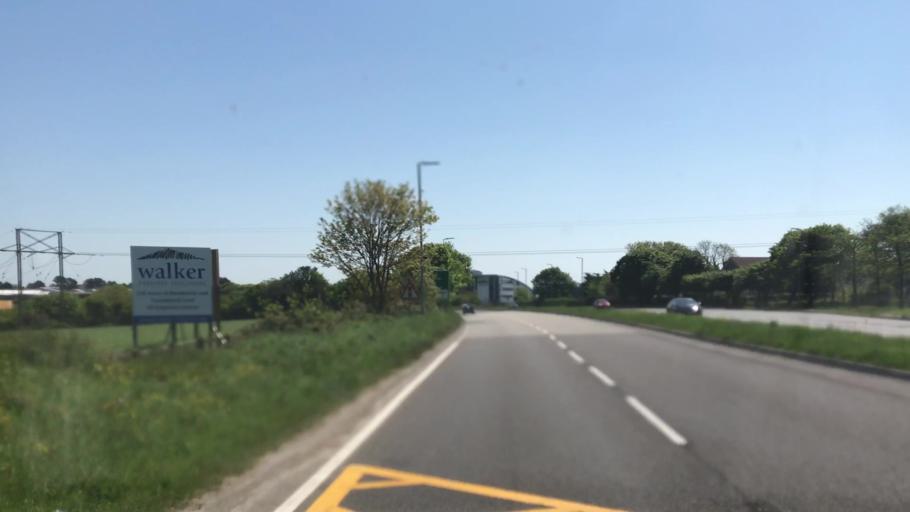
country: GB
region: England
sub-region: Cornwall
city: Truro
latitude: 50.2639
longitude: -5.1090
